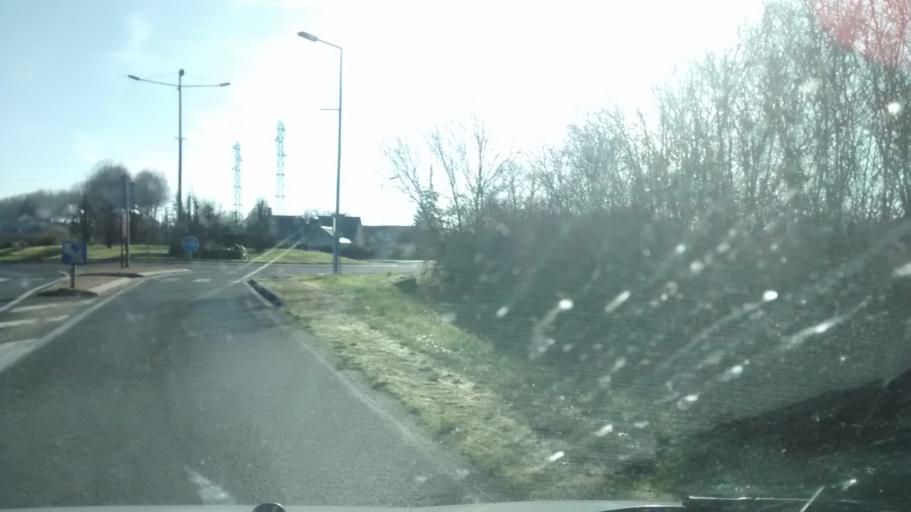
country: FR
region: Centre
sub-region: Departement d'Indre-et-Loire
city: Nazelles-Negron
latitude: 47.4281
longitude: 0.9586
